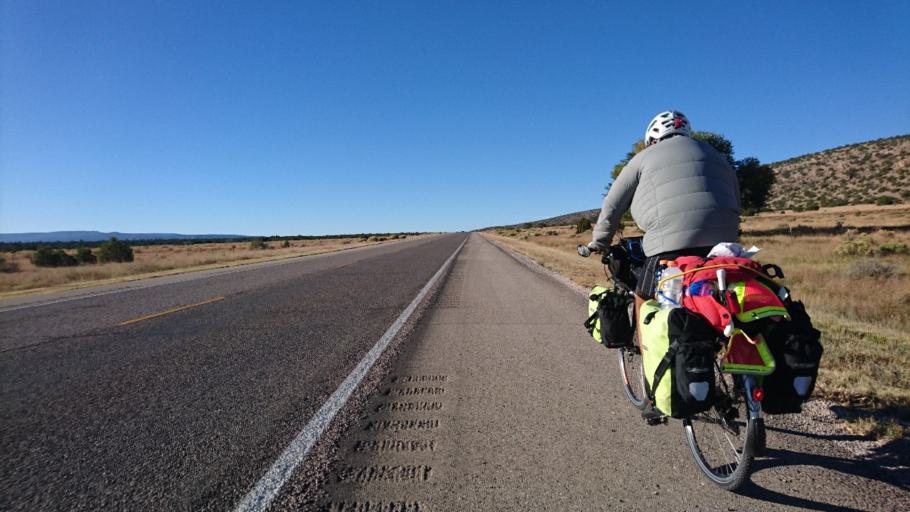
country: US
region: New Mexico
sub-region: Cibola County
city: Grants
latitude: 34.9901
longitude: -107.9012
